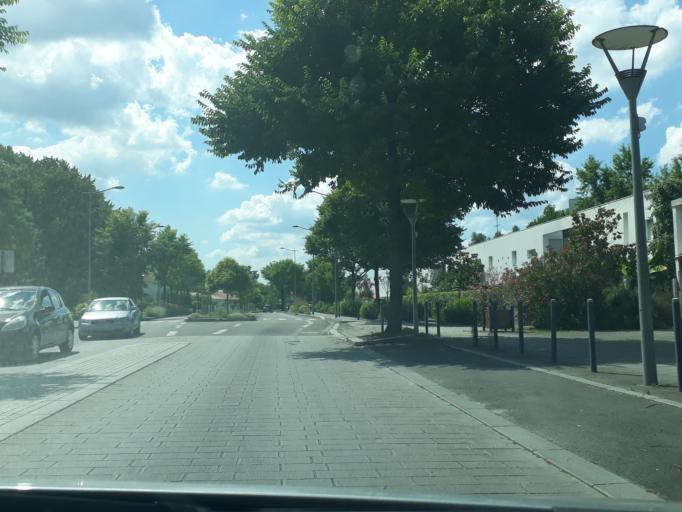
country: FR
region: Aquitaine
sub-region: Departement de la Gironde
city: Merignac
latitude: 44.8416
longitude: -0.6569
